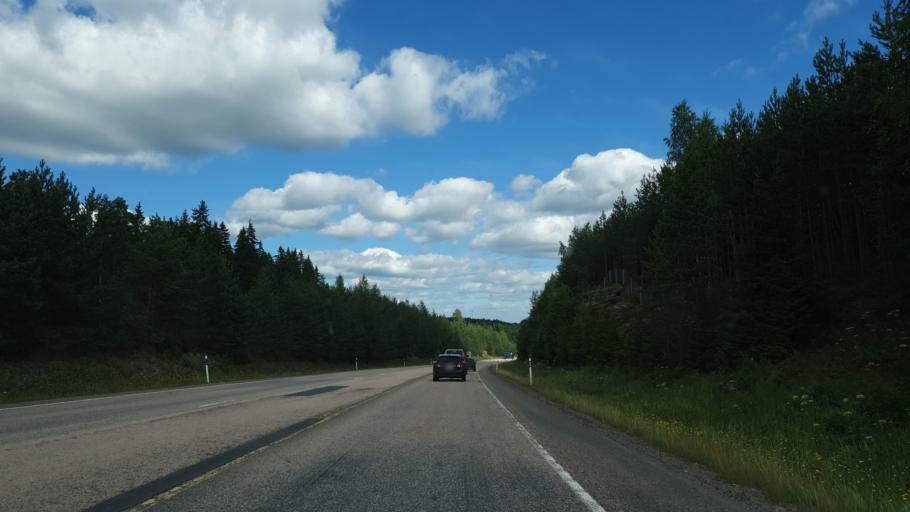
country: FI
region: Central Finland
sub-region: Jaemsae
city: Jaemsae
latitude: 61.8312
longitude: 25.0887
